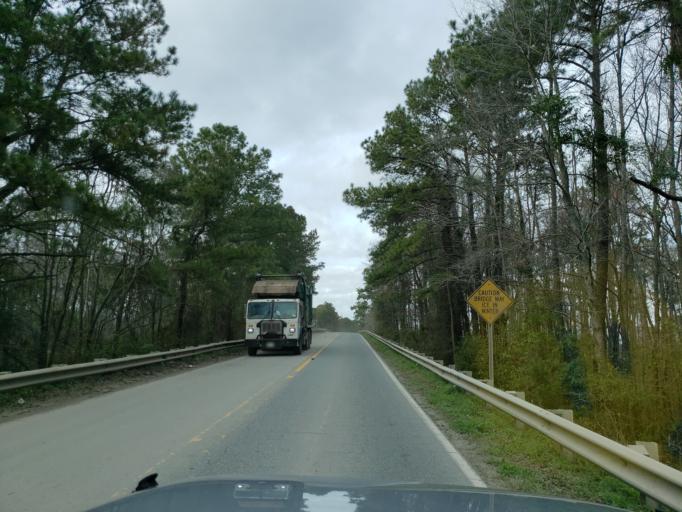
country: US
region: Georgia
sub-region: Chatham County
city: Georgetown
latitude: 32.0265
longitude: -81.2682
